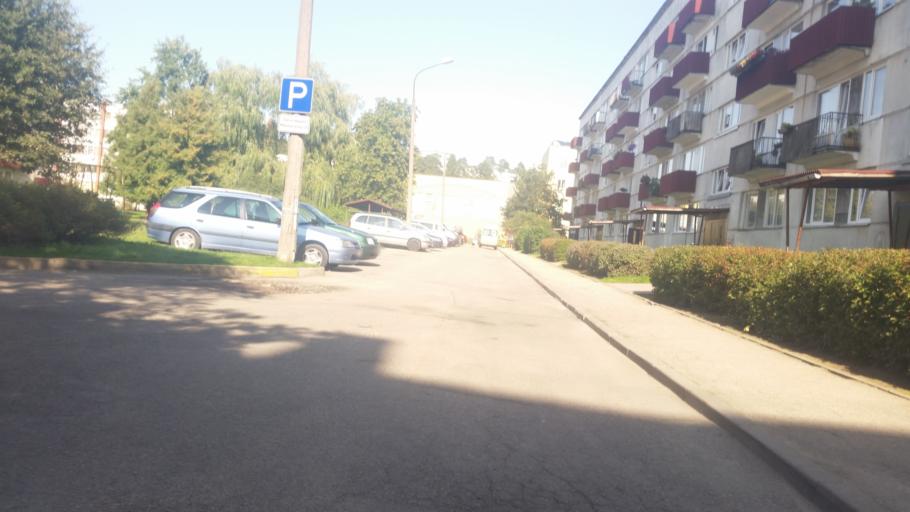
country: LV
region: Ogre
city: Ogre
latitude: 56.8214
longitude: 24.5989
